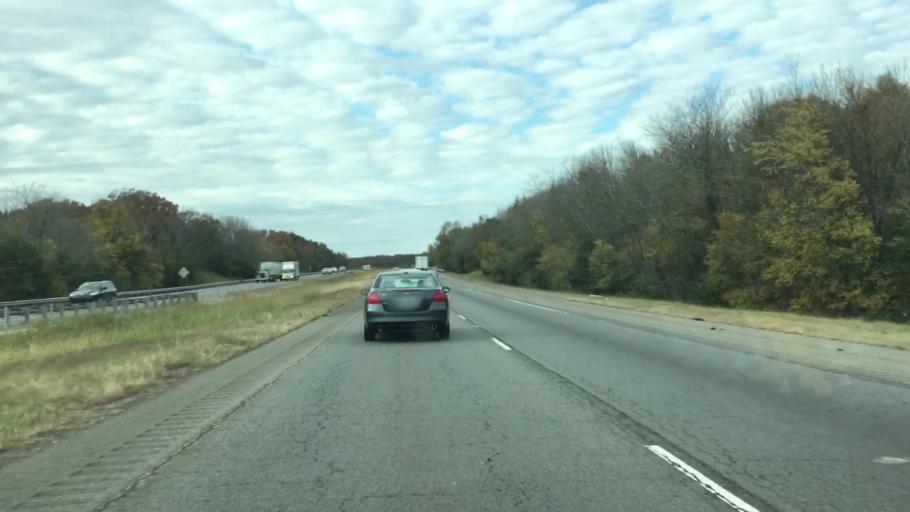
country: US
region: Arkansas
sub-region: Faulkner County
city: Conway
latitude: 35.1315
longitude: -92.5156
